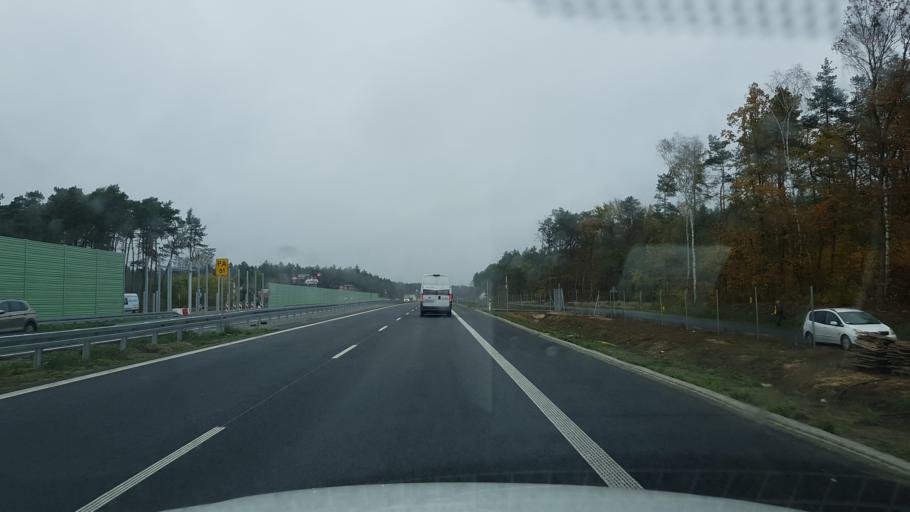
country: PL
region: West Pomeranian Voivodeship
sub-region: Powiat goleniowski
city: Goleniow
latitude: 53.4618
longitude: 14.7882
